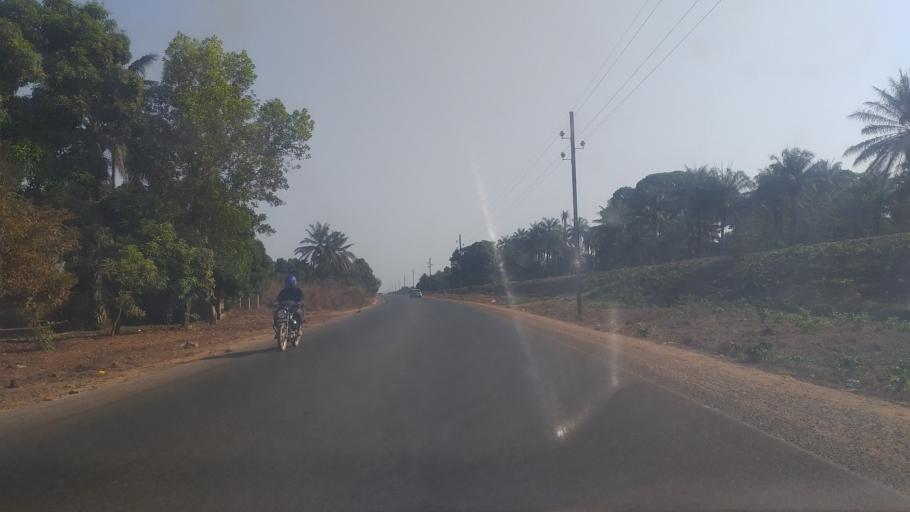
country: GN
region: Boke
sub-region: Boke Prefecture
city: Kamsar
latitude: 10.7133
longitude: -14.5229
